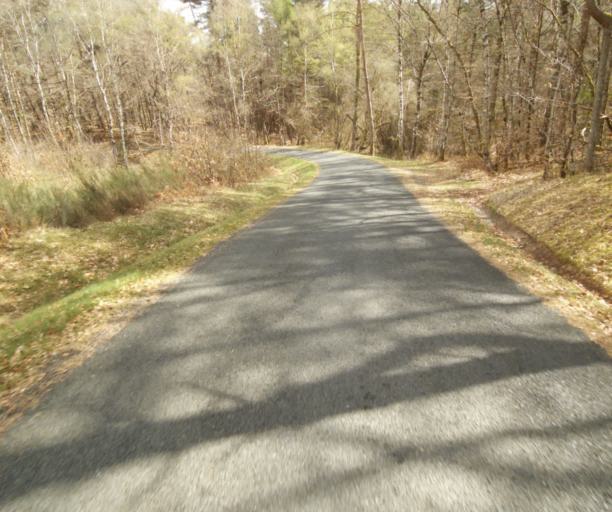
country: FR
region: Limousin
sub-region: Departement de la Correze
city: Correze
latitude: 45.2791
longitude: 1.8989
